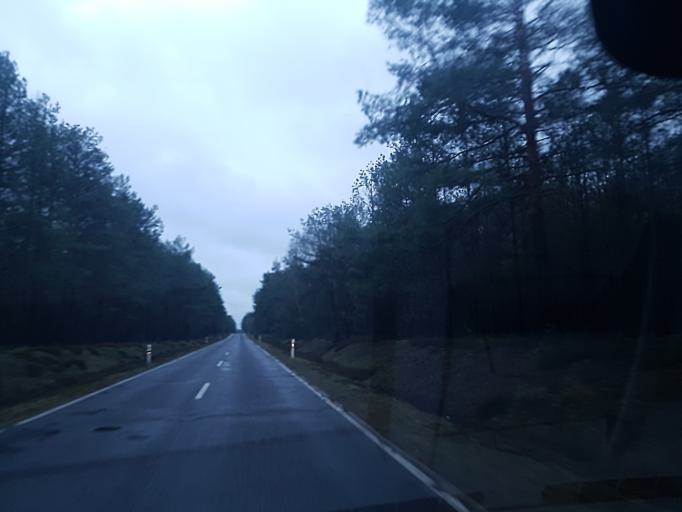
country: DE
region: Brandenburg
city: Schonewalde
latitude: 51.6212
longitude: 13.6382
